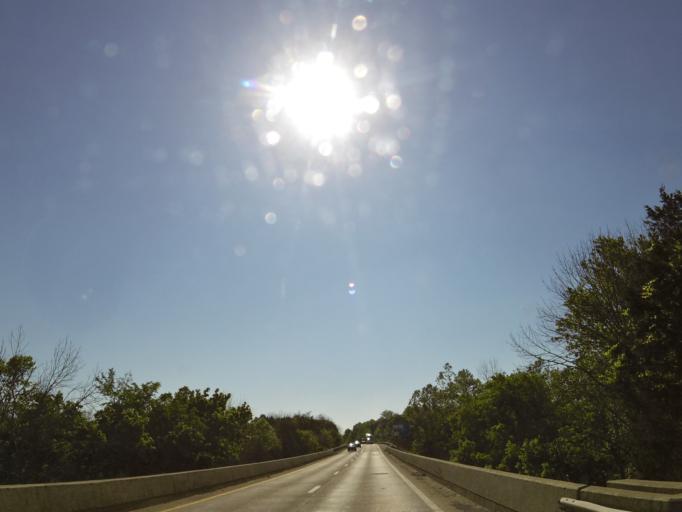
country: US
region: Kentucky
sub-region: Franklin County
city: Frankfort
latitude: 38.1446
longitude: -85.0005
